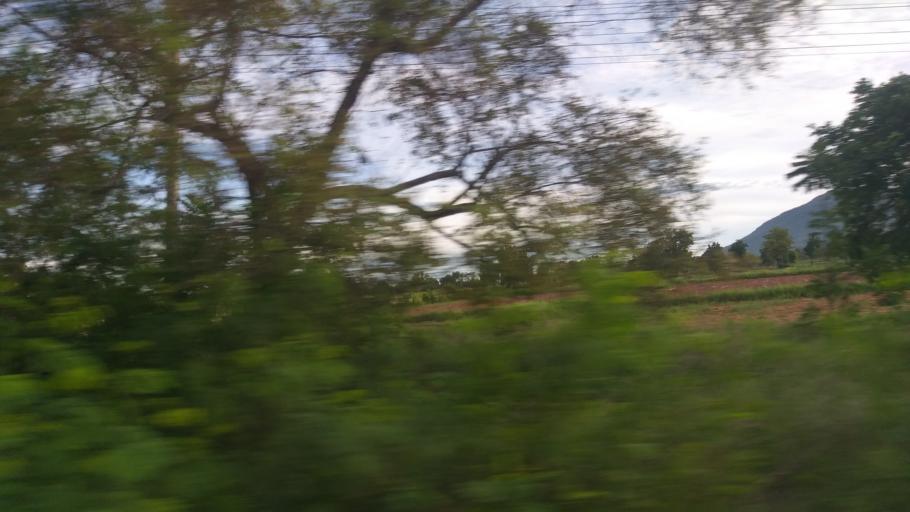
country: TH
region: Chaiyaphum
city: Phu Khiao
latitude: 16.3311
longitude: 102.2221
